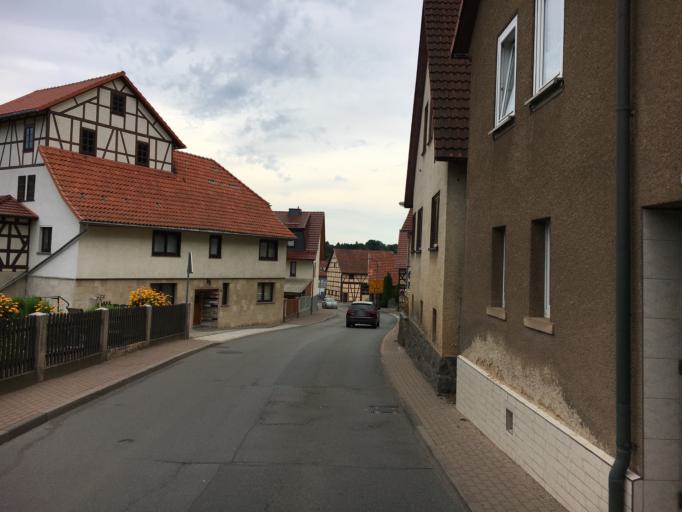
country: DE
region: Thuringia
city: Trusetal
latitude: 50.7884
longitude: 10.4086
